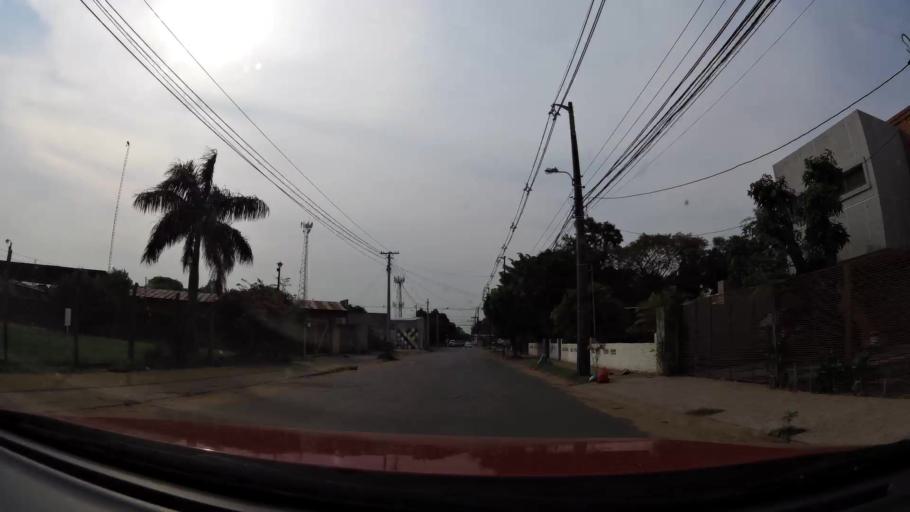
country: PY
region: Asuncion
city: Asuncion
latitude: -25.2617
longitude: -57.5802
